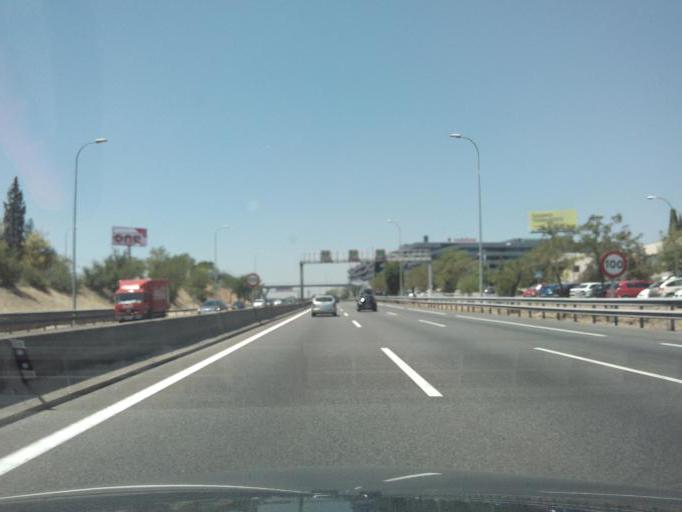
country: ES
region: Madrid
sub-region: Provincia de Madrid
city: San Blas
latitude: 40.4501
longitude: -3.5981
